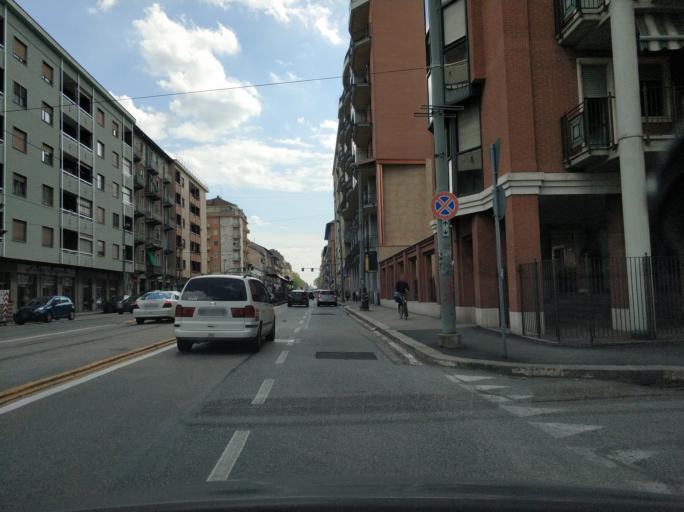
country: IT
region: Piedmont
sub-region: Provincia di Torino
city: Turin
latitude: 45.0986
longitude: 7.6978
